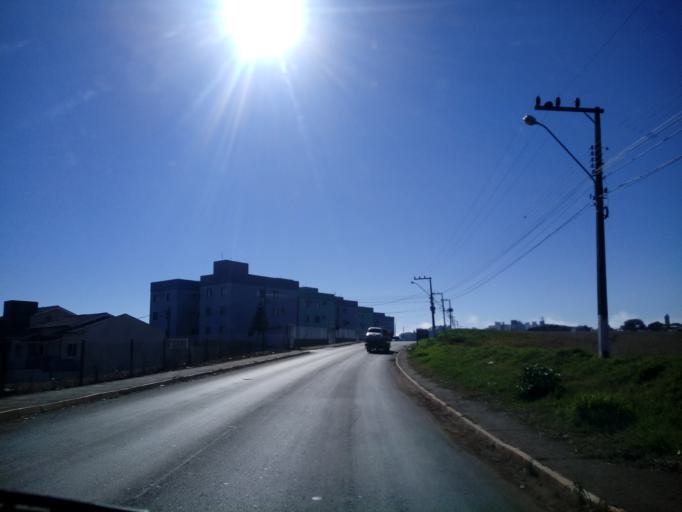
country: BR
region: Santa Catarina
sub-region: Chapeco
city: Chapeco
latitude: -27.0711
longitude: -52.6104
